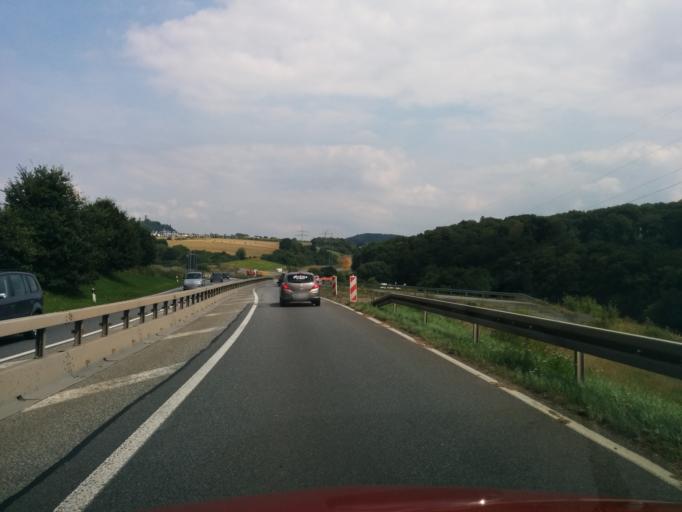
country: DE
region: Hesse
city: Merenberg
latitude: 50.4914
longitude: 8.1743
